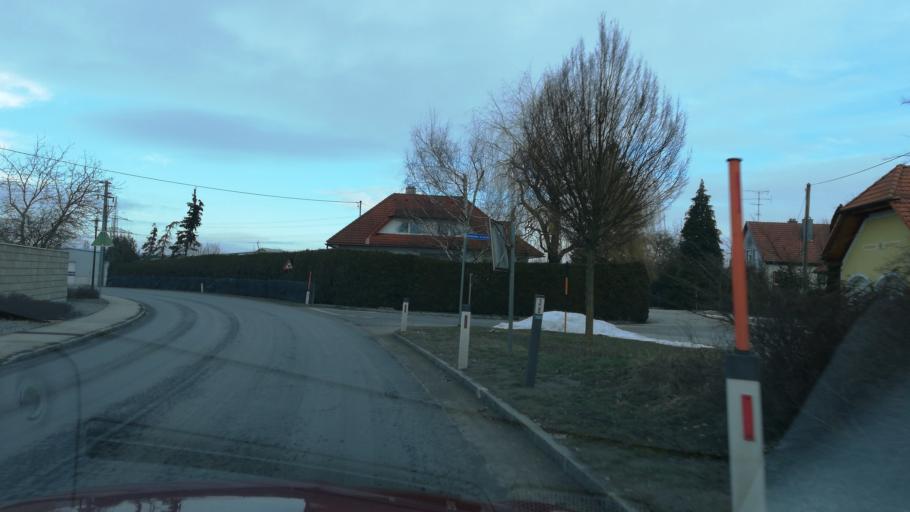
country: AT
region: Upper Austria
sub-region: Politischer Bezirk Vocklabruck
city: Wolfsegg am Hausruck
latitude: 48.1767
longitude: 13.6948
